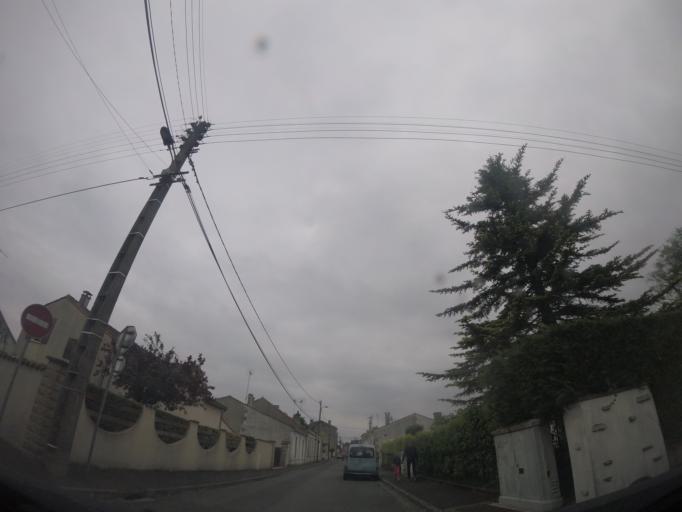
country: FR
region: Poitou-Charentes
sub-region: Departement de la Charente
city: Cognac
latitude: 45.6920
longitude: -0.3271
